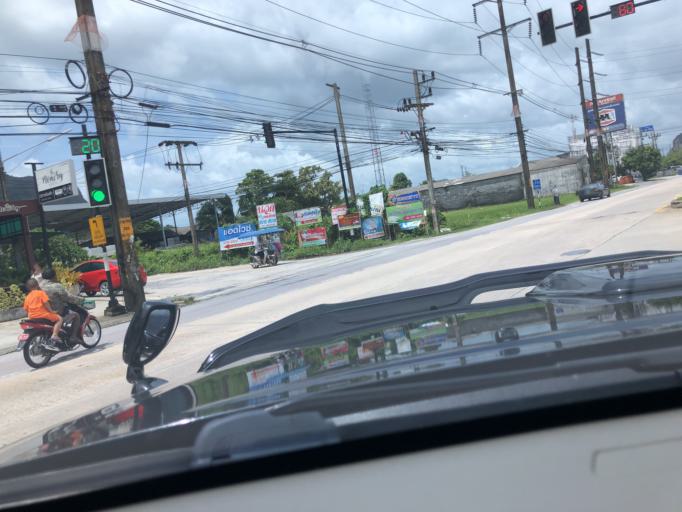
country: TH
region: Phangnga
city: Phang Nga
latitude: 8.4459
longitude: 98.5306
